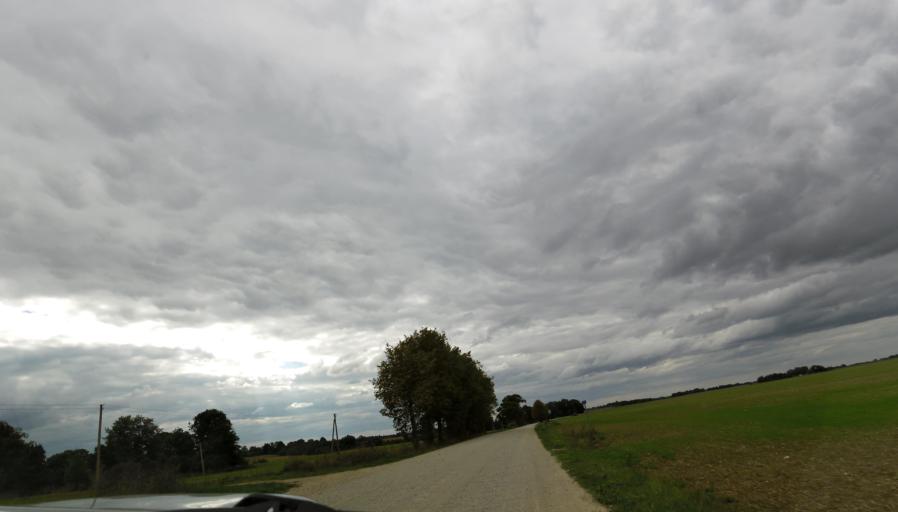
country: LT
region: Panevezys
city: Pasvalys
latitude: 56.0601
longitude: 24.2733
